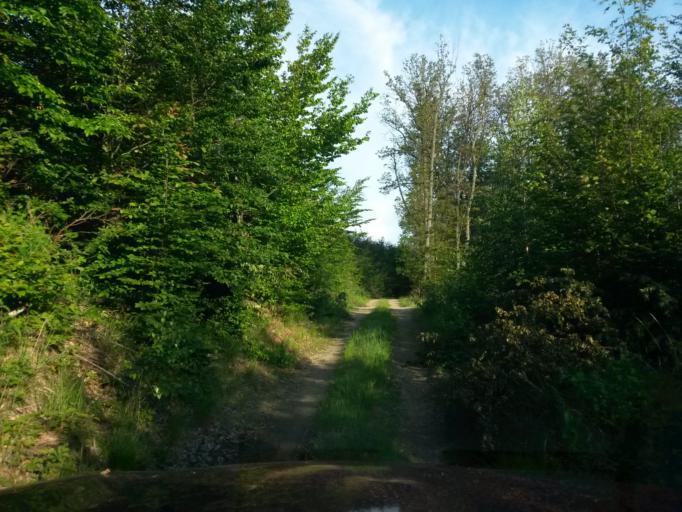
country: SK
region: Kosicky
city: Moldava nad Bodvou
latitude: 48.7368
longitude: 21.0389
